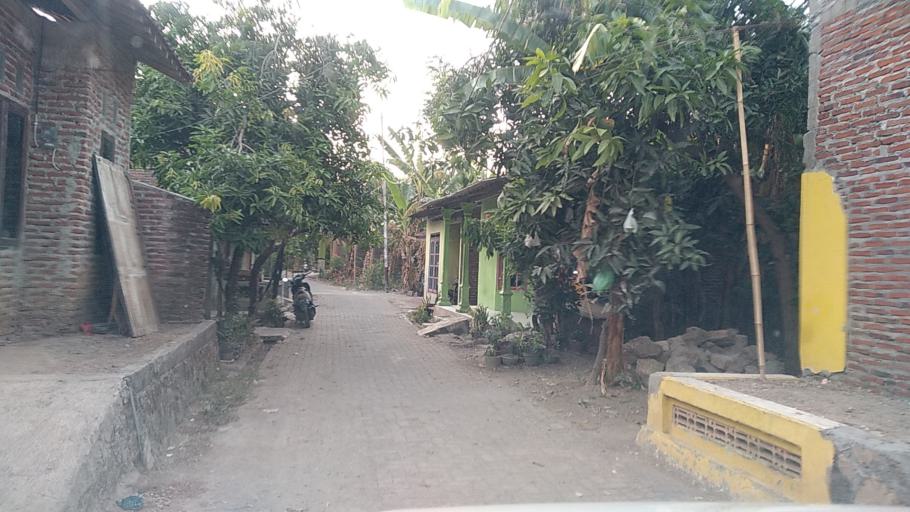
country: ID
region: Central Java
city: Semarang
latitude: -6.9675
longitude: 110.2916
